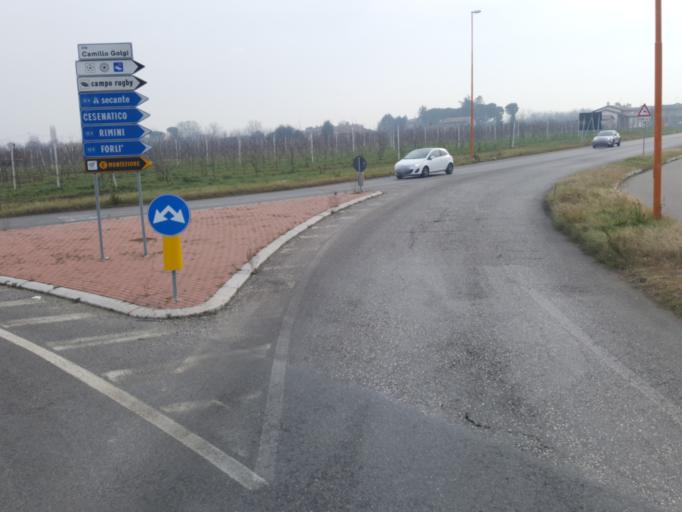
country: IT
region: Emilia-Romagna
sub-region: Forli-Cesena
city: Cesena
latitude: 44.1554
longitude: 12.2690
